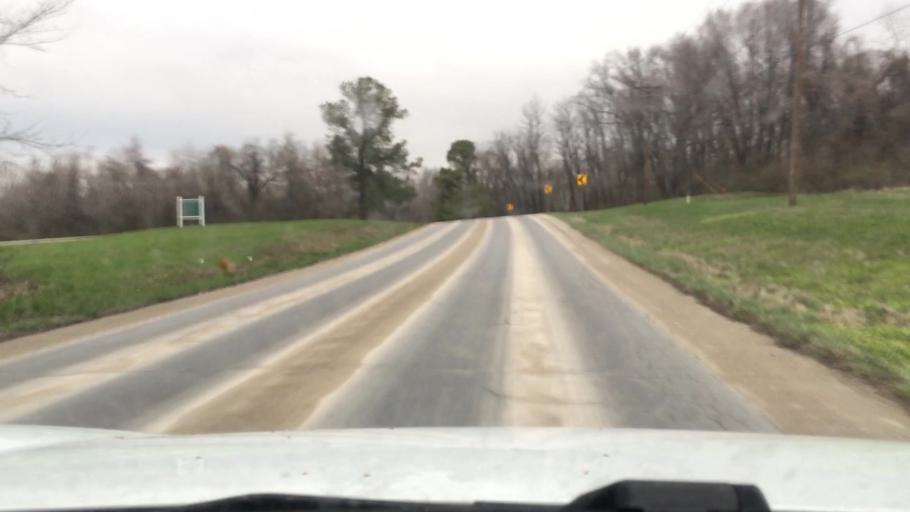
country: US
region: Missouri
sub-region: Saint Charles County
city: Weldon Spring
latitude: 38.6684
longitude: -90.7325
